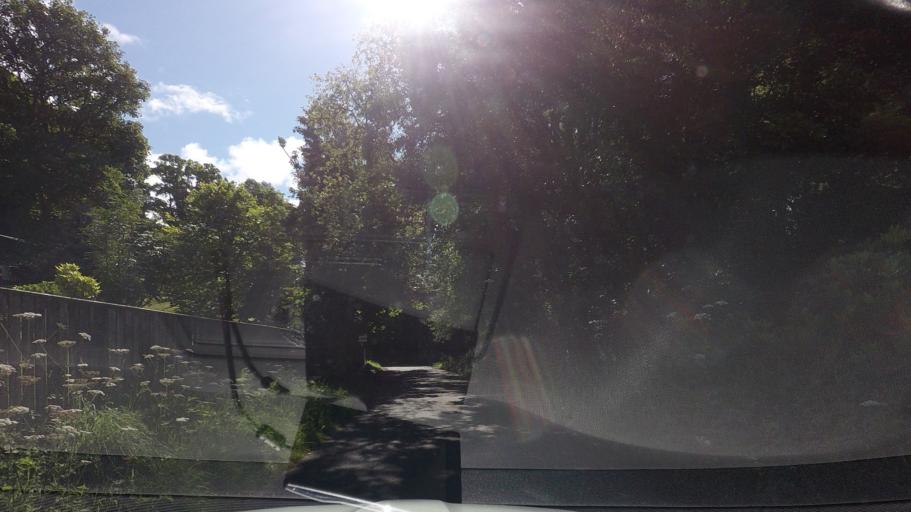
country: GB
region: Scotland
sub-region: Stirling
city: Killearn
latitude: 56.0645
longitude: -4.4734
